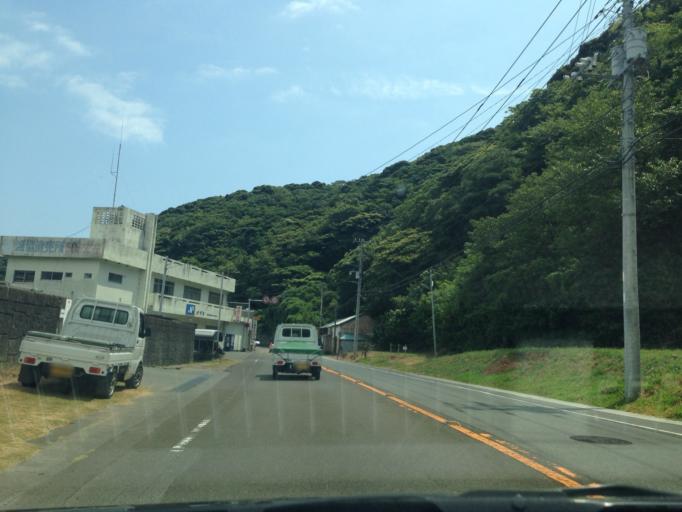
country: JP
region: Shizuoka
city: Shimoda
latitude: 34.6308
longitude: 138.8856
